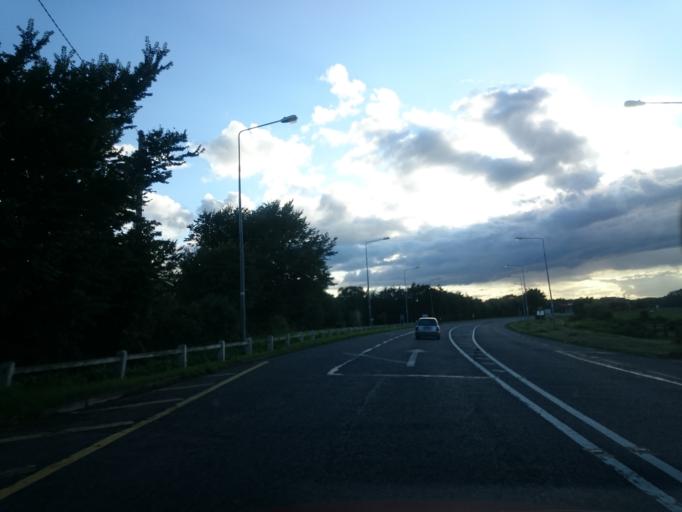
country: IE
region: Leinster
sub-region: Loch Garman
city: Rosslare
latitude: 52.2569
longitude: -6.4503
